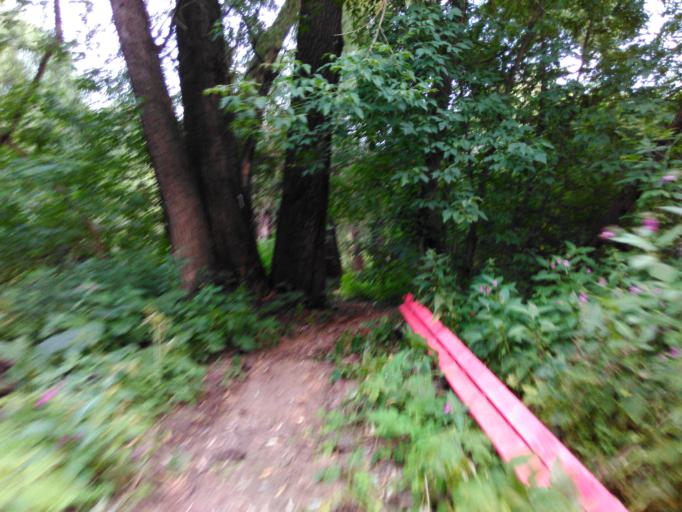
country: RU
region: Moscow
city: Davydkovo
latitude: 55.7199
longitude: 37.4861
